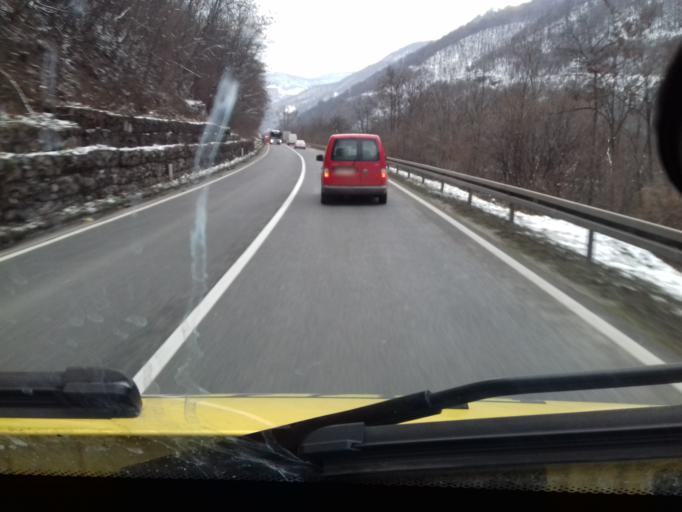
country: BA
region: Federation of Bosnia and Herzegovina
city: Lokvine
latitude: 44.2800
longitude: 17.8828
